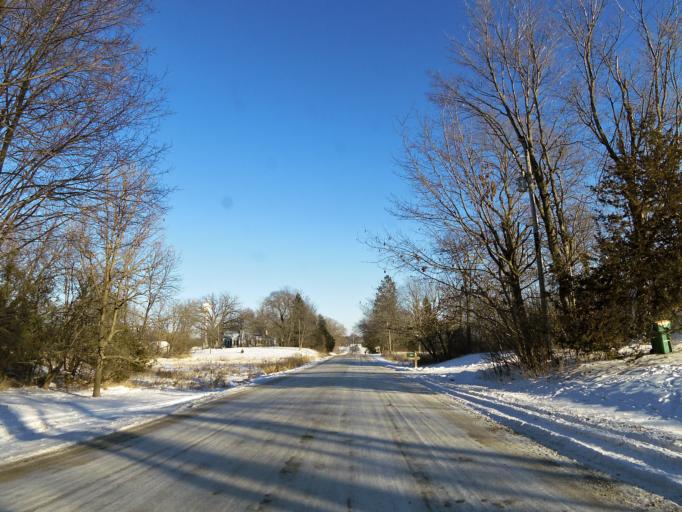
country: US
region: Minnesota
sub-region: Hennepin County
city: Mound
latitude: 44.9568
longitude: -93.6778
